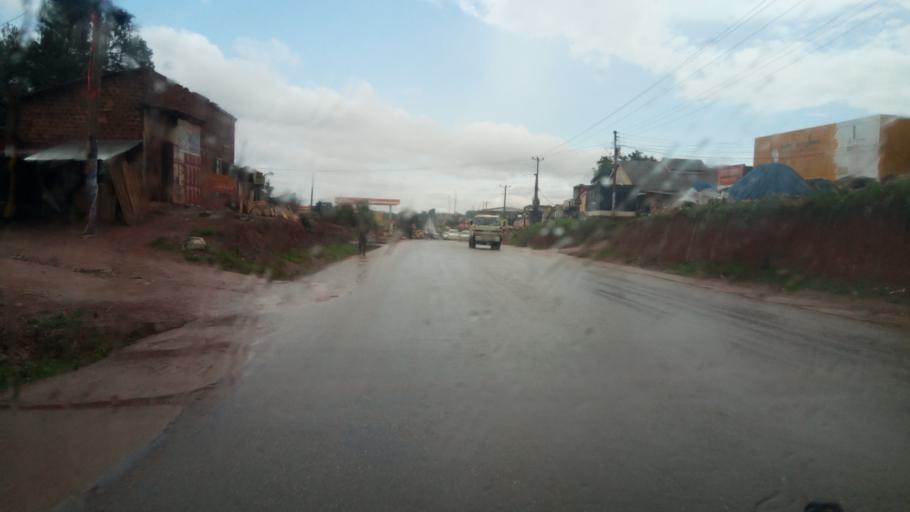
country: UG
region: Central Region
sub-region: Wakiso District
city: Wakiso
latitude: 0.3801
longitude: 32.5195
